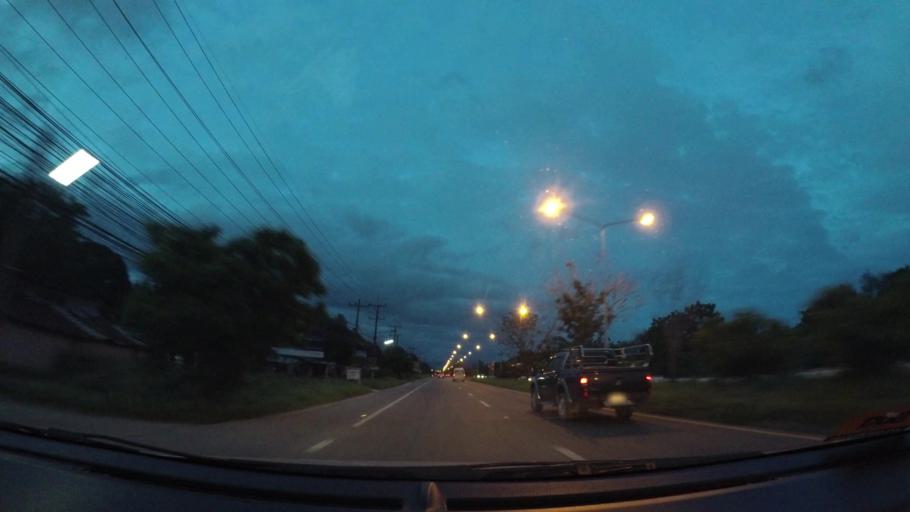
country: TH
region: Rayong
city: Ban Chang
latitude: 12.6936
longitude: 100.9869
